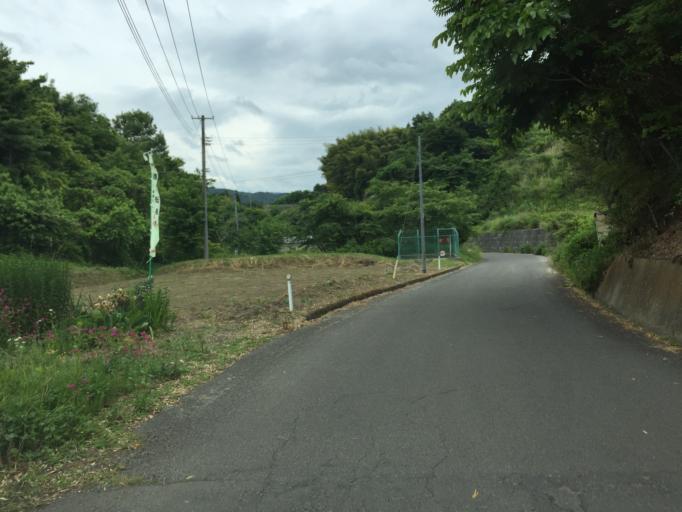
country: JP
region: Fukushima
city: Miharu
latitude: 37.3973
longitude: 140.5361
